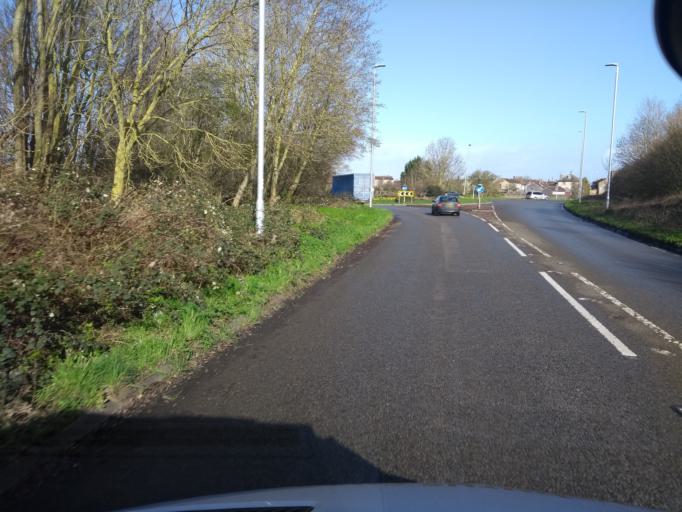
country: GB
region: England
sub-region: Somerset
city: Ilchester
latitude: 50.9977
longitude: -2.6814
